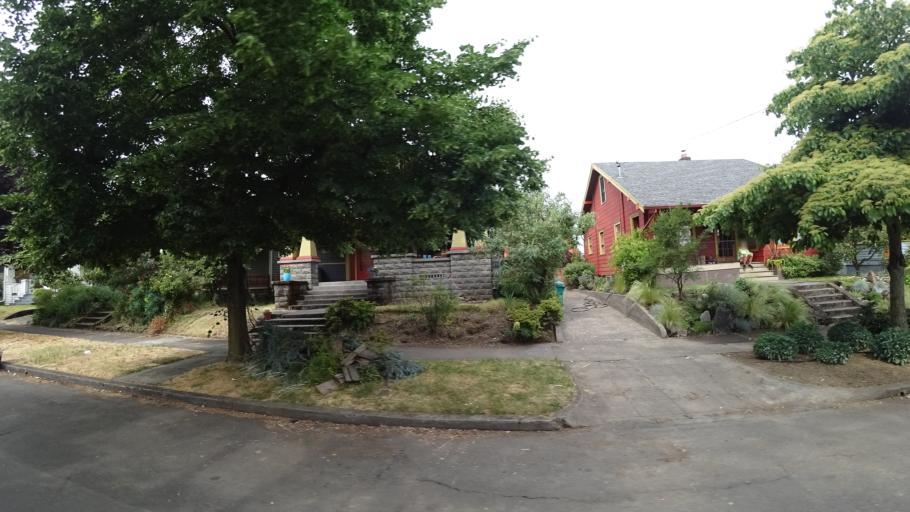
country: US
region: Oregon
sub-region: Multnomah County
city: Portland
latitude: 45.5730
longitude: -122.6759
